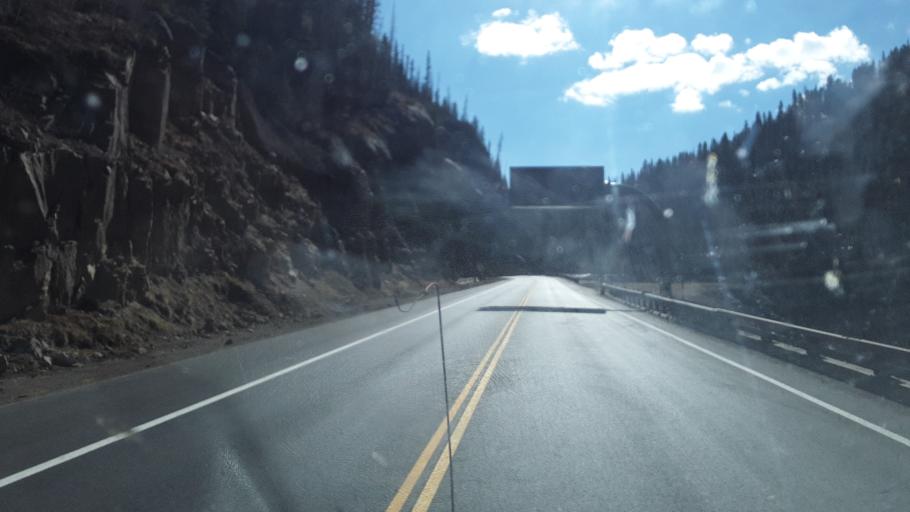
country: US
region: Colorado
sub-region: Mineral County
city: Creede
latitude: 37.5509
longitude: -106.7760
